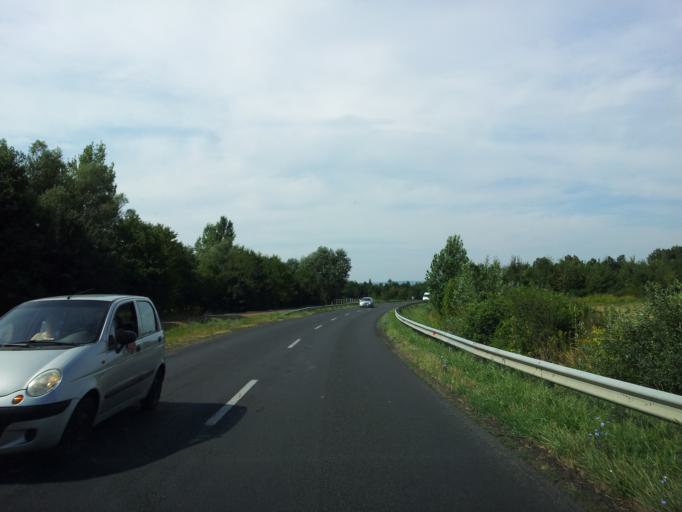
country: HU
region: Veszprem
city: Tapolca
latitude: 46.8842
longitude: 17.4849
